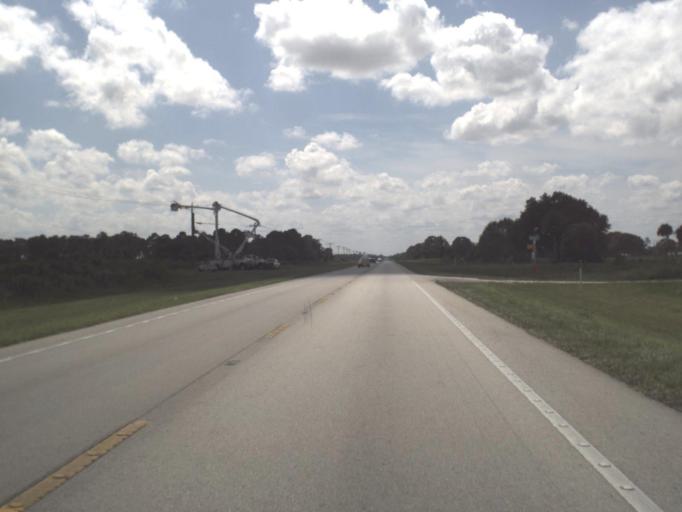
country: US
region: Florida
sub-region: Collier County
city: Immokalee
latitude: 26.4710
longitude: -81.4344
